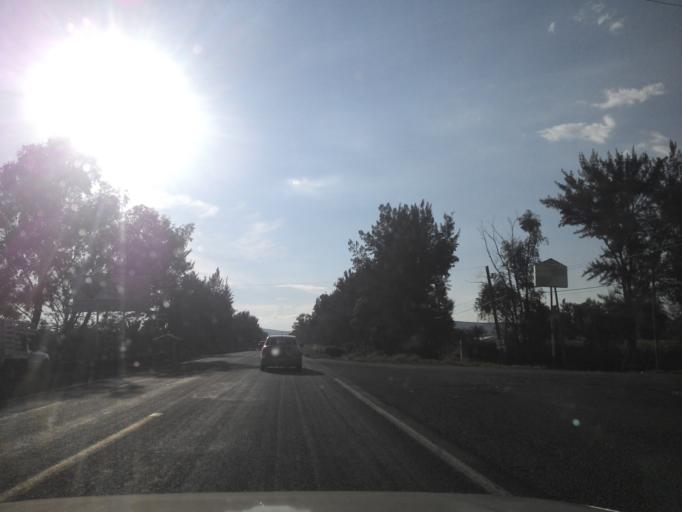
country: MX
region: Jalisco
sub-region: Tototlan
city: Nuevo Refugio de Afuera (Nuevo Refugio)
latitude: 20.5579
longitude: -102.7195
